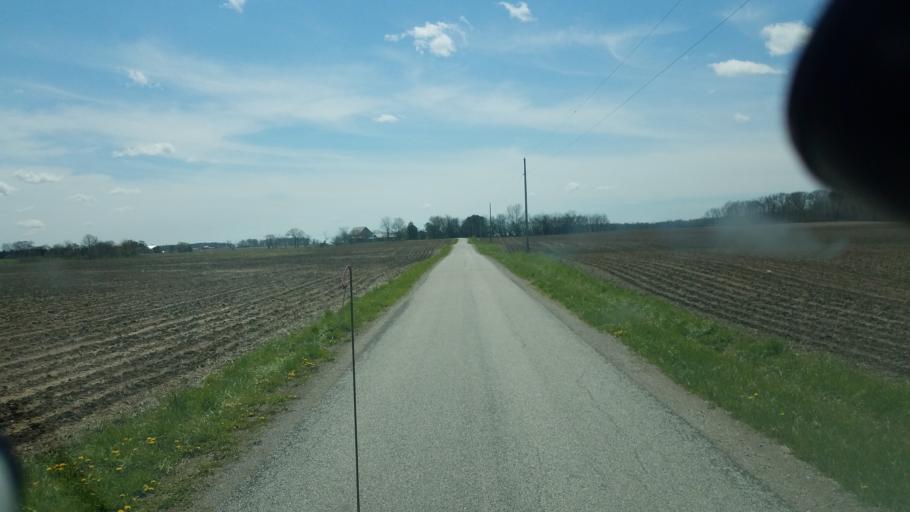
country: US
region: Ohio
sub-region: Union County
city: Richwood
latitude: 40.5142
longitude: -83.2887
